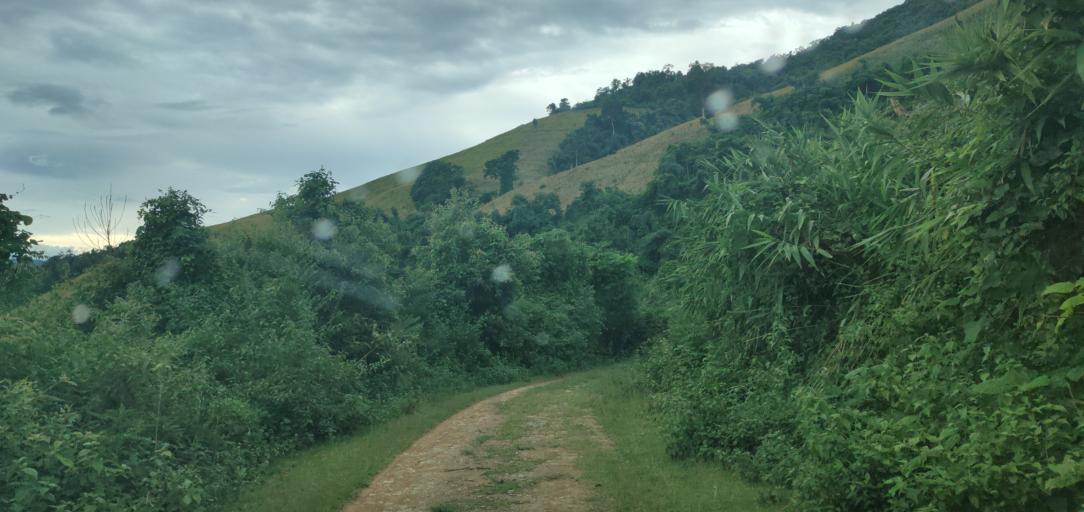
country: LA
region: Phongsali
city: Phongsali
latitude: 21.4395
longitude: 102.3292
